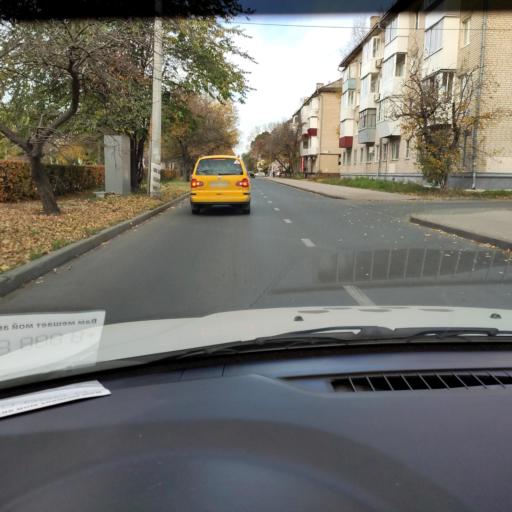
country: RU
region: Samara
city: Tol'yatti
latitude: 53.5064
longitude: 49.4127
